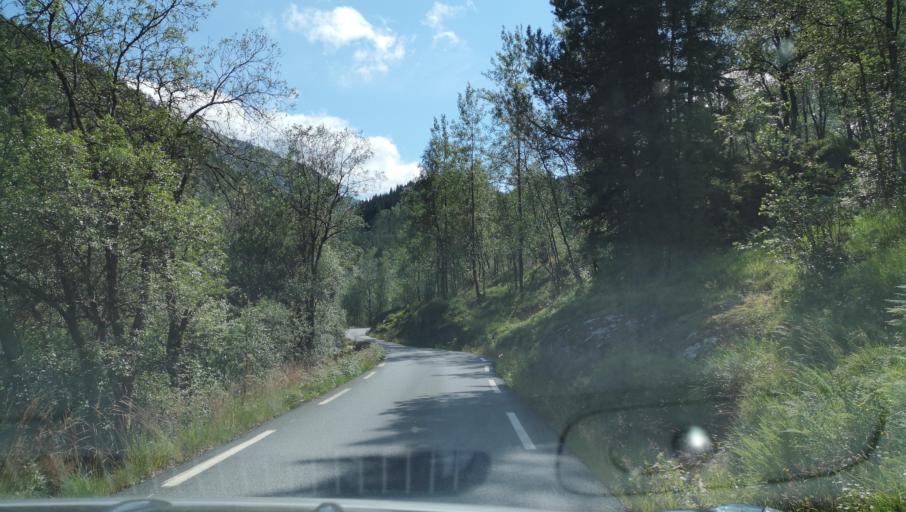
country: NO
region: Hordaland
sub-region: Modalen
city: Mo
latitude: 60.7826
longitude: 5.9478
